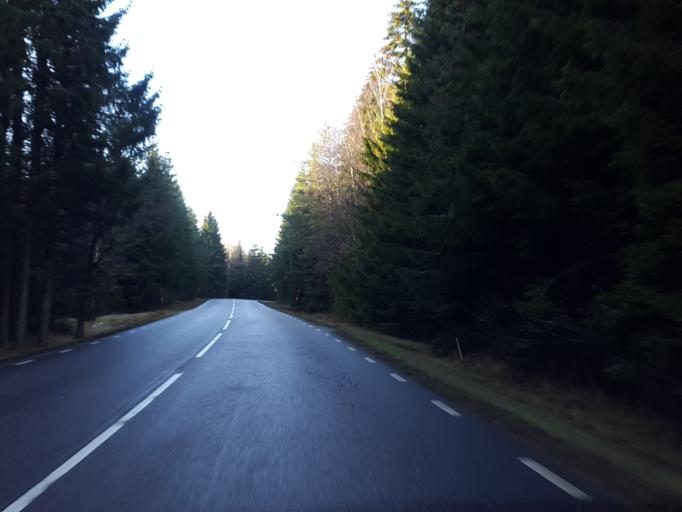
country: SE
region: Vaestra Goetaland
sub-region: Herrljunga Kommun
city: Herrljunga
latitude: 57.9903
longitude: 12.9725
